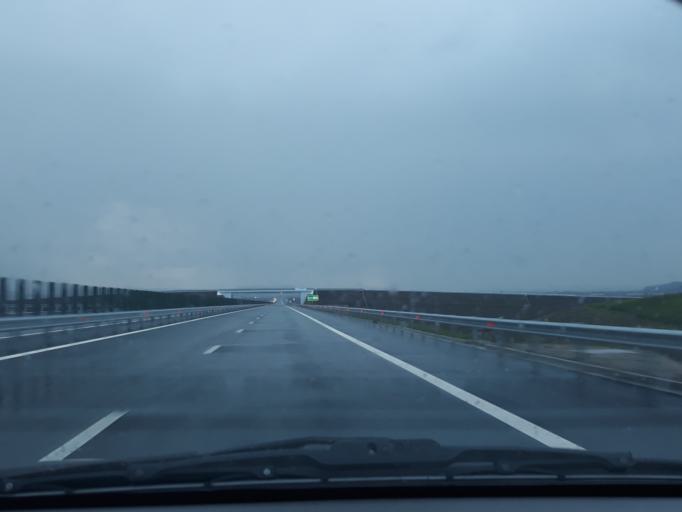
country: RO
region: Mures
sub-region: Comuna Ogra
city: Ogra
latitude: 46.4374
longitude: 24.3250
